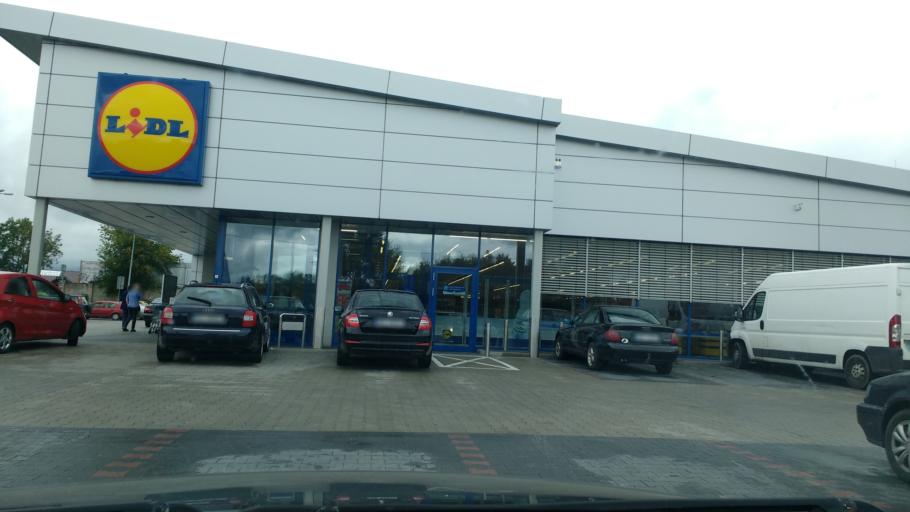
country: PL
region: Pomeranian Voivodeship
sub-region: Powiat kartuski
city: Chwaszczyno
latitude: 54.4432
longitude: 18.4133
